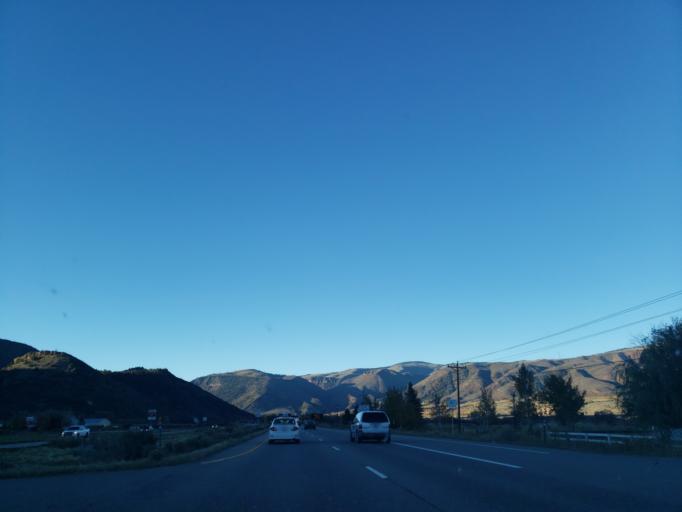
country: US
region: Colorado
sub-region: Pitkin County
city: Snowmass Village
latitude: 39.2543
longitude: -106.8853
